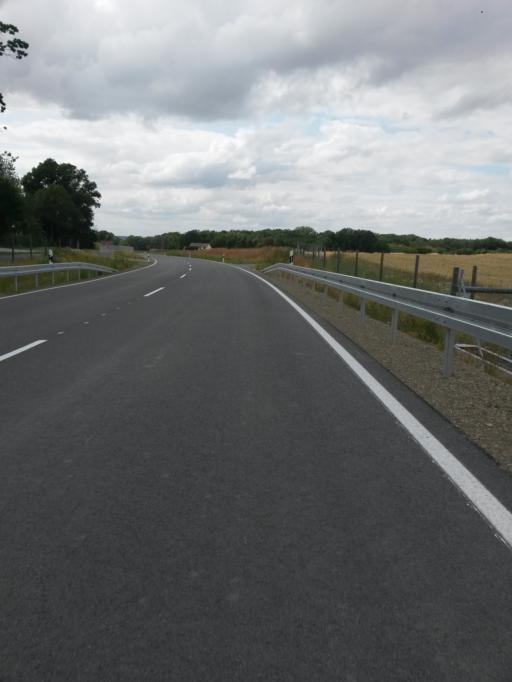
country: DE
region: North Rhine-Westphalia
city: Bad Oeynhausen
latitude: 52.1613
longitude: 8.7626
